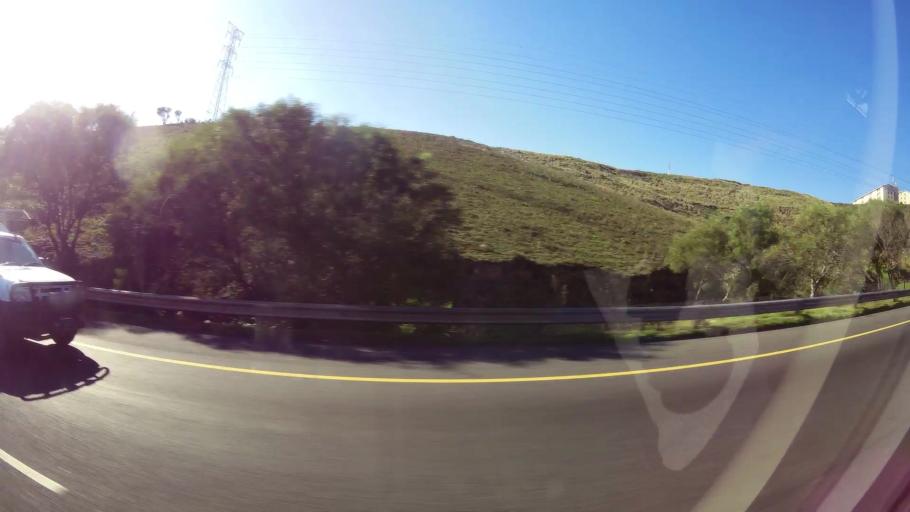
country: ZA
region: Eastern Cape
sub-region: Nelson Mandela Bay Metropolitan Municipality
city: Port Elizabeth
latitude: -33.9319
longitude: 25.5577
